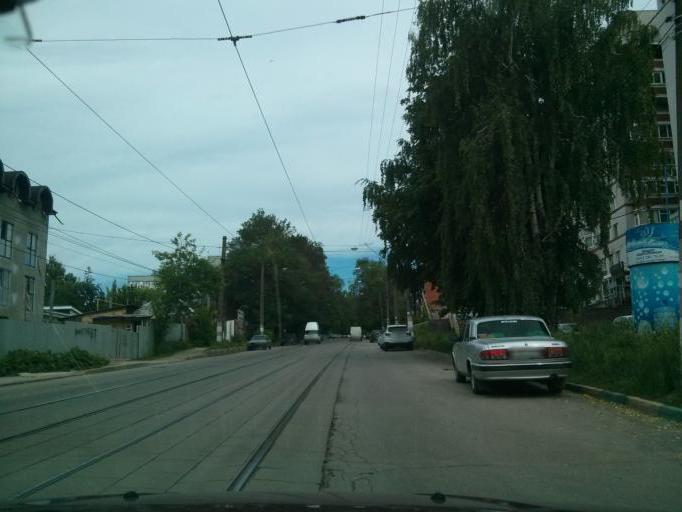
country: RU
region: Nizjnij Novgorod
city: Nizhniy Novgorod
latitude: 56.3066
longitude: 44.0201
